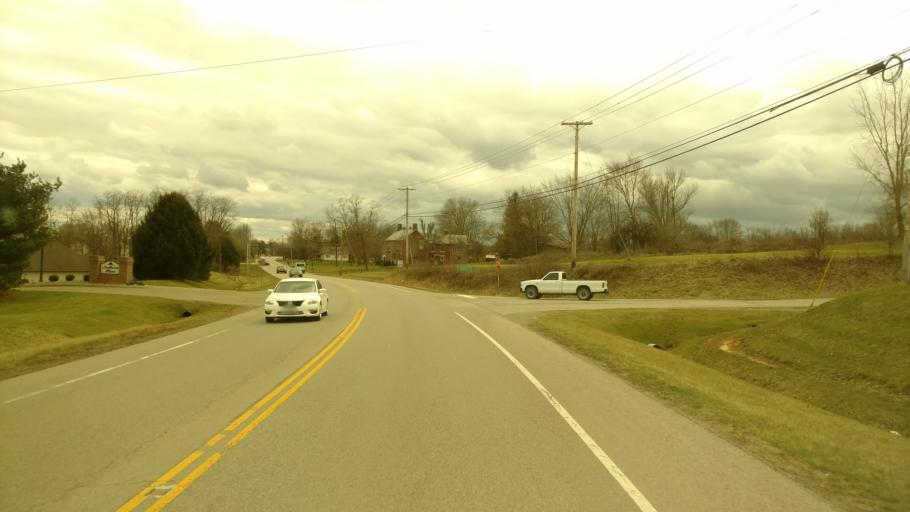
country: US
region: Ohio
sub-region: Muskingum County
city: North Zanesville
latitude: 40.0194
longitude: -82.0418
